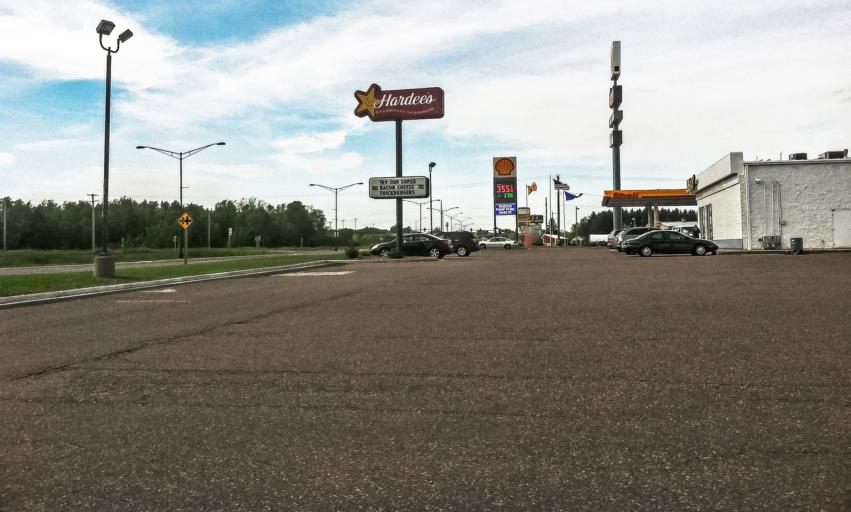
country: US
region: Wisconsin
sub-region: Clark County
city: Colby
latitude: 44.9280
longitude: -90.3150
